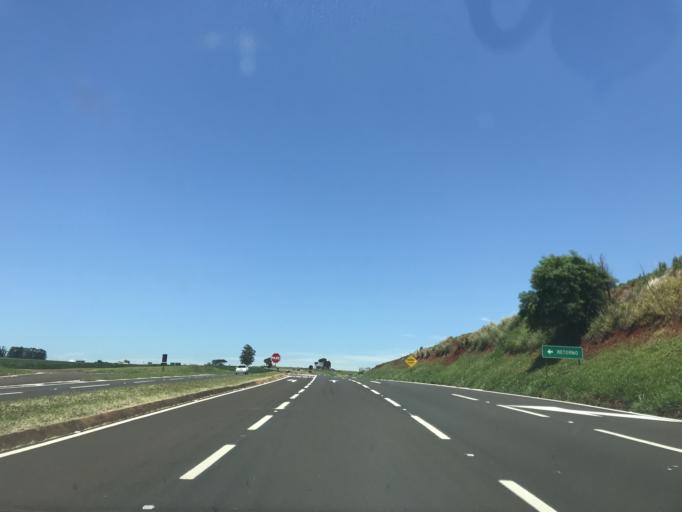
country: BR
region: Parana
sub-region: Rolandia
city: Rolandia
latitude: -23.3399
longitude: -51.3606
